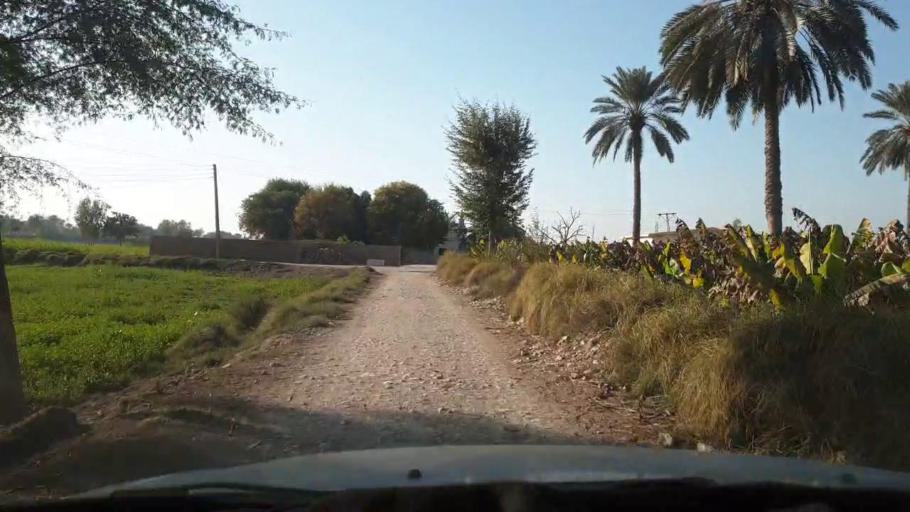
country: PK
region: Sindh
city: Adilpur
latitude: 27.9561
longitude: 69.2323
